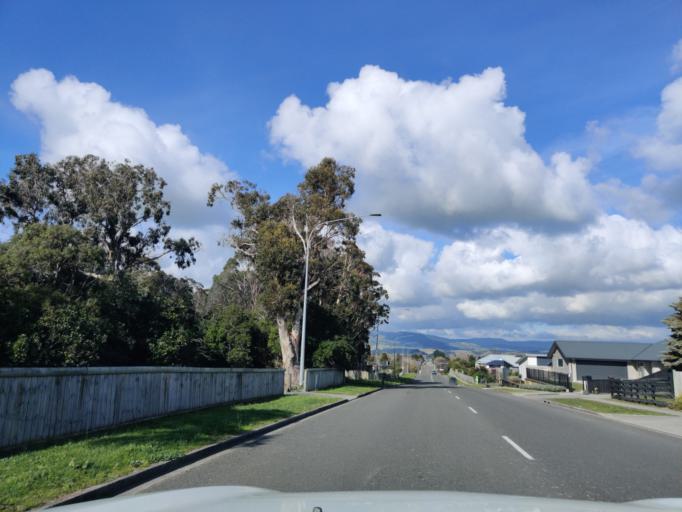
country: NZ
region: Manawatu-Wanganui
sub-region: Palmerston North City
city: Palmerston North
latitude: -40.3211
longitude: 175.6587
